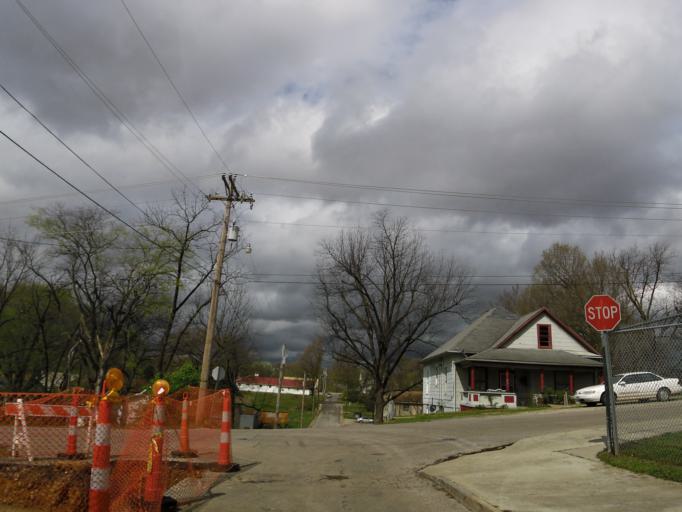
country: US
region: Missouri
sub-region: Butler County
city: Poplar Bluff
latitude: 36.7541
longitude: -90.3977
